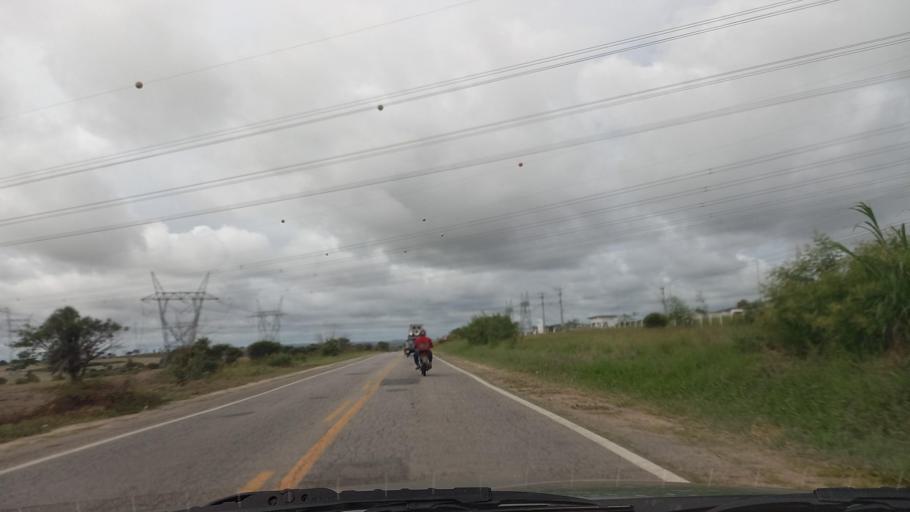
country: BR
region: Pernambuco
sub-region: Sao Joao
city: Sao Joao
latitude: -8.8802
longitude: -36.4037
